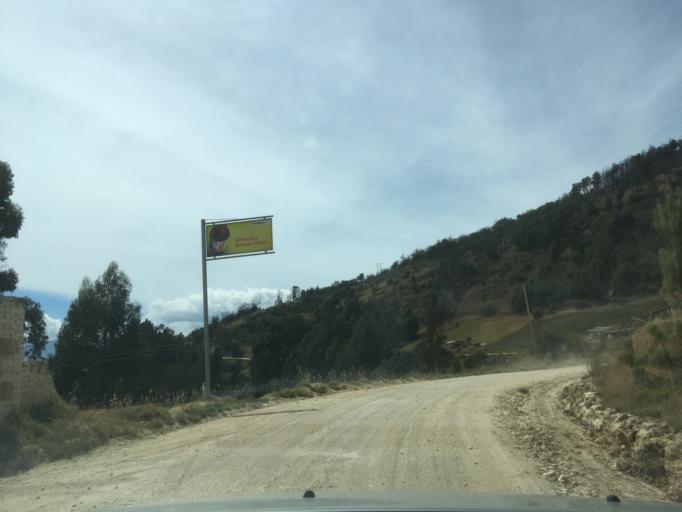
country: CO
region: Boyaca
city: Aquitania
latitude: 5.5913
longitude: -72.9198
